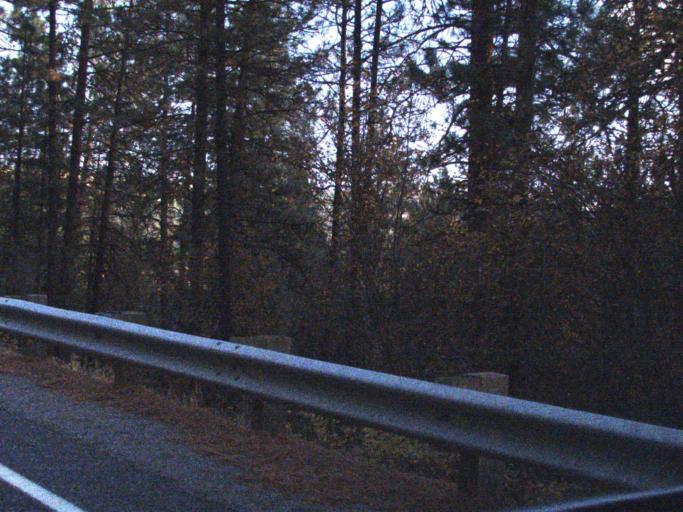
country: US
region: Washington
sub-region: Stevens County
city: Kettle Falls
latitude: 48.7242
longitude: -118.0391
